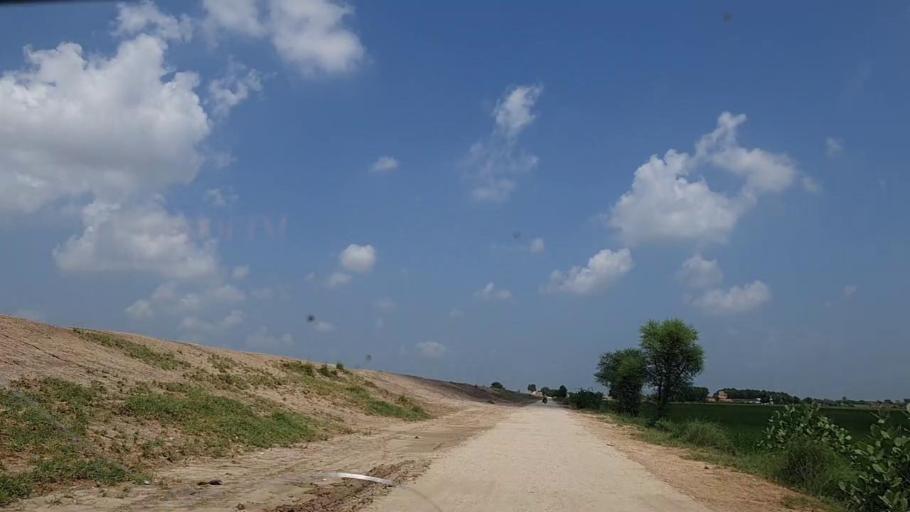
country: PK
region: Sindh
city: Tharu Shah
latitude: 26.9893
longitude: 68.0640
